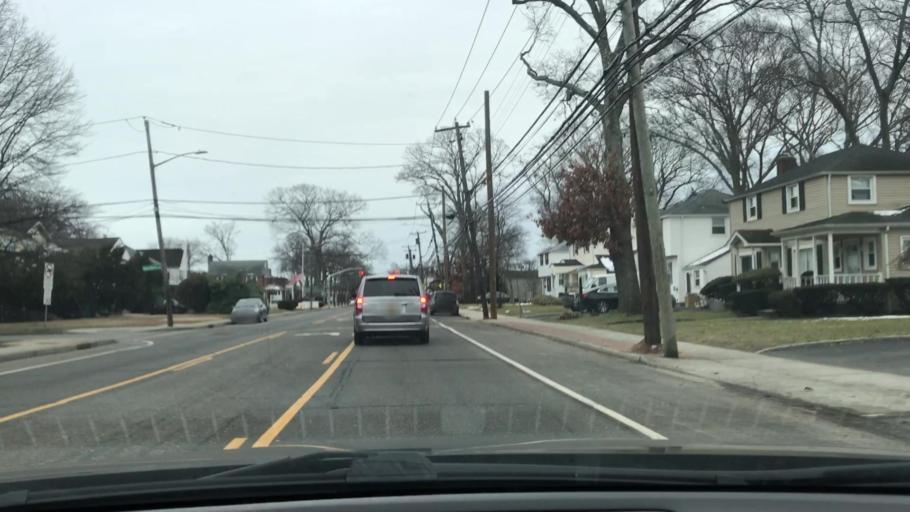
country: US
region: New York
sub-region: Nassau County
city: Merrick
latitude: 40.6697
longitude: -73.5547
